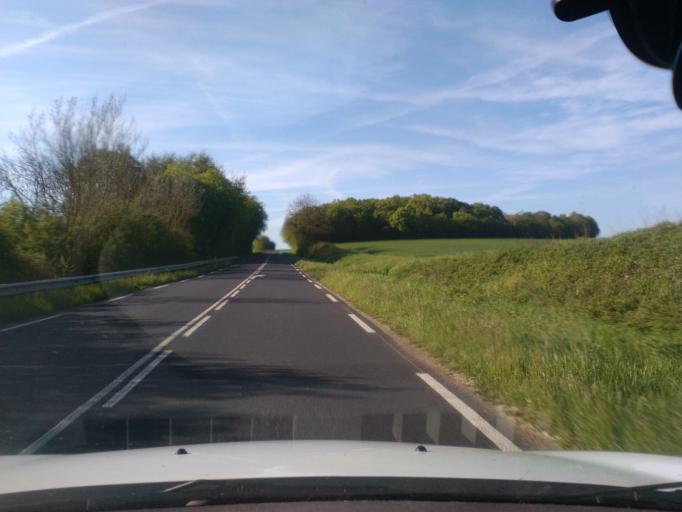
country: FR
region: Lorraine
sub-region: Departement des Vosges
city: Mirecourt
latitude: 48.3399
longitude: 6.1397
